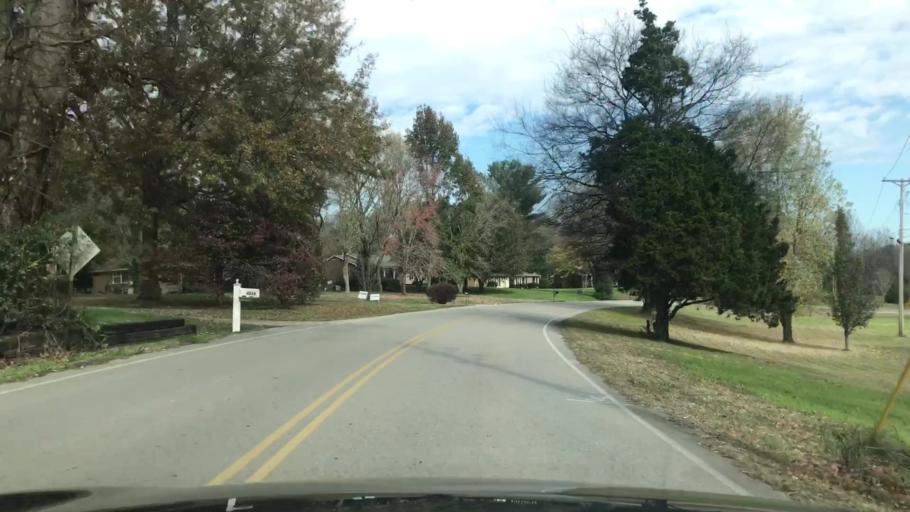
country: US
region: Tennessee
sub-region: Williamson County
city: Franklin
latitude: 35.9129
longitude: -86.8115
